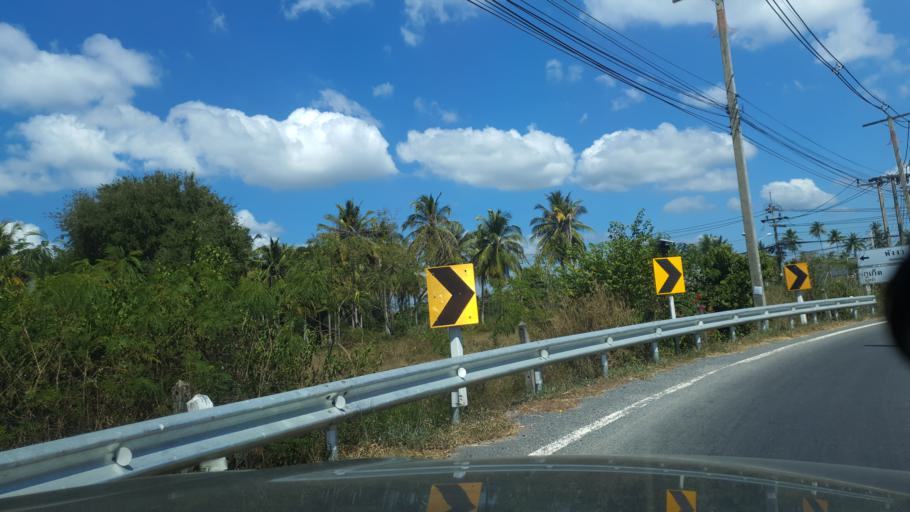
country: TH
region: Phuket
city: Thalang
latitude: 8.1588
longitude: 98.3040
